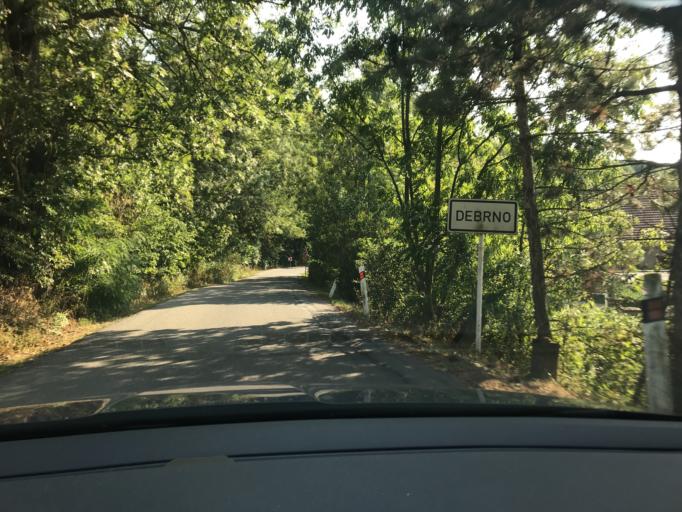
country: CZ
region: Central Bohemia
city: Kralupy nad Vltavou
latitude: 50.2184
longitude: 14.3281
